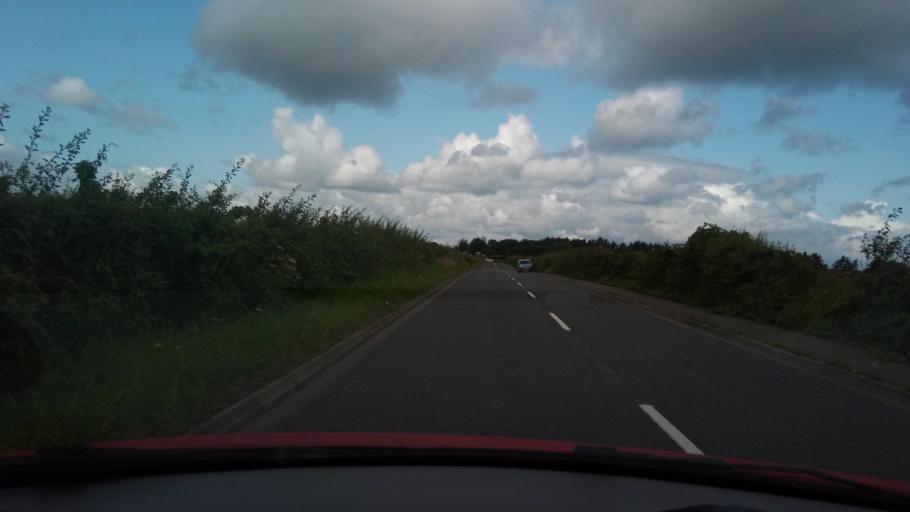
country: GB
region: Scotland
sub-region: East Lothian
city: Tranent
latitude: 55.9360
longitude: -2.9375
